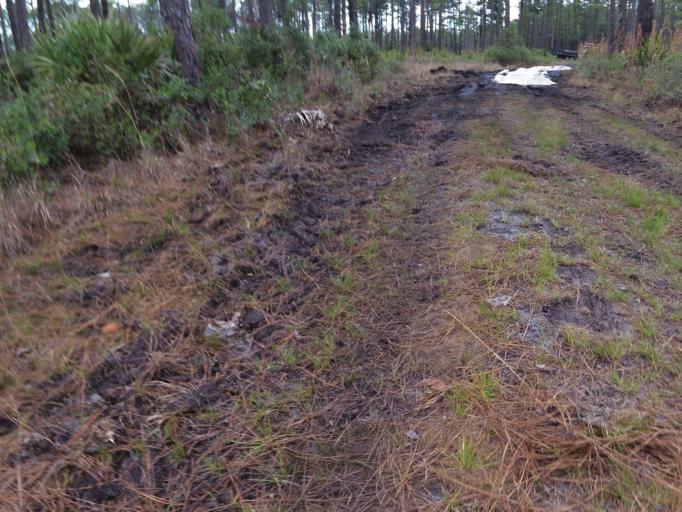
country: US
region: Florida
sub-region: Duval County
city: Atlantic Beach
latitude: 30.4778
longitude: -81.5005
